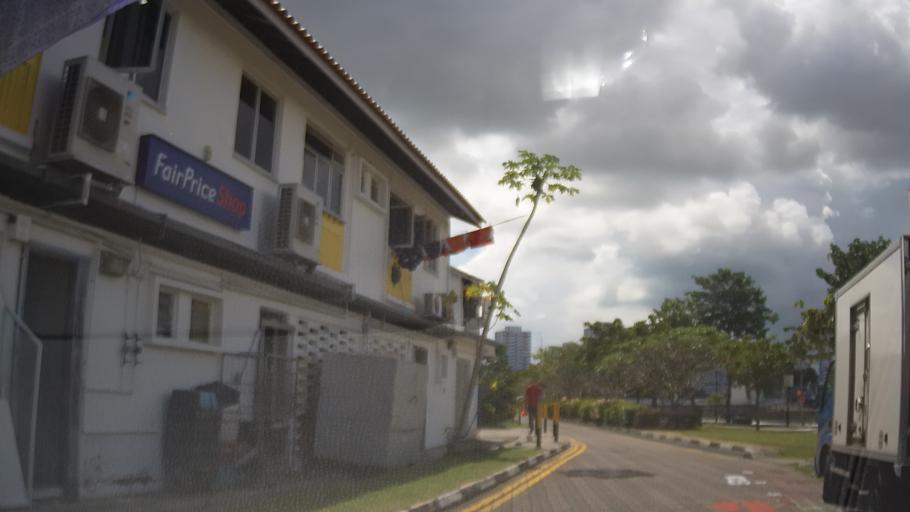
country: SG
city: Singapore
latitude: 1.3286
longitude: 103.8855
